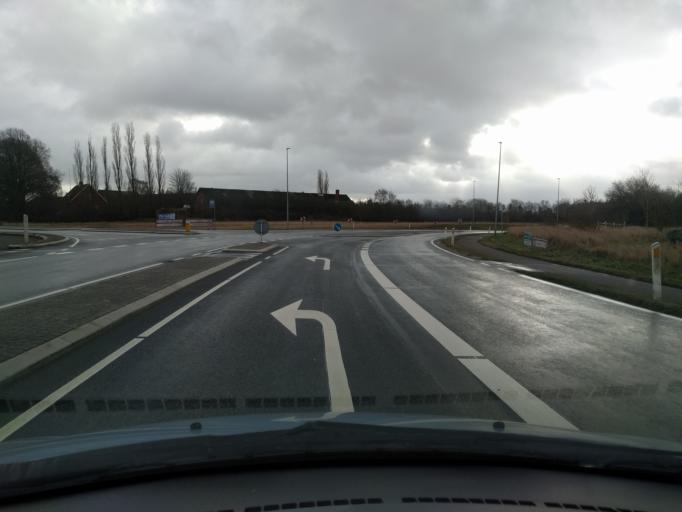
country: DK
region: South Denmark
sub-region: Kerteminde Kommune
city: Langeskov
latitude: 55.3664
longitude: 10.5745
